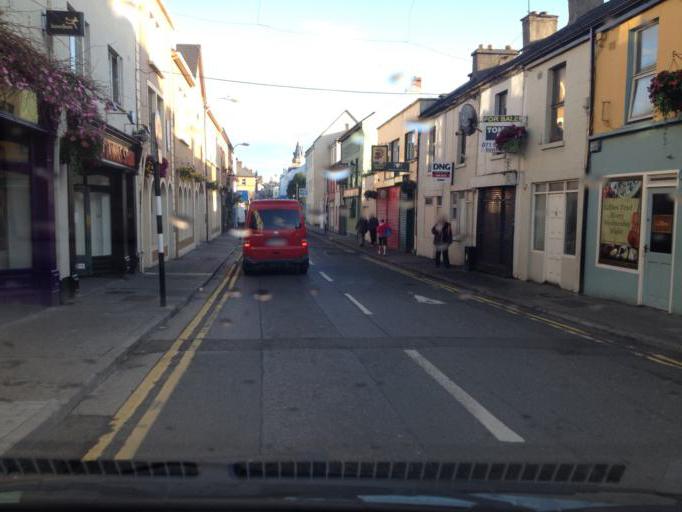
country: IE
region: Connaught
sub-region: Sligo
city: Sligo
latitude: 54.2726
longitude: -8.4715
